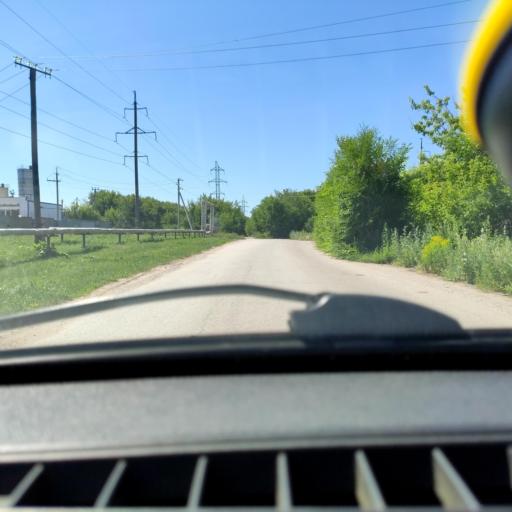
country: RU
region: Samara
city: Tol'yatti
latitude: 53.5752
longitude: 49.2994
